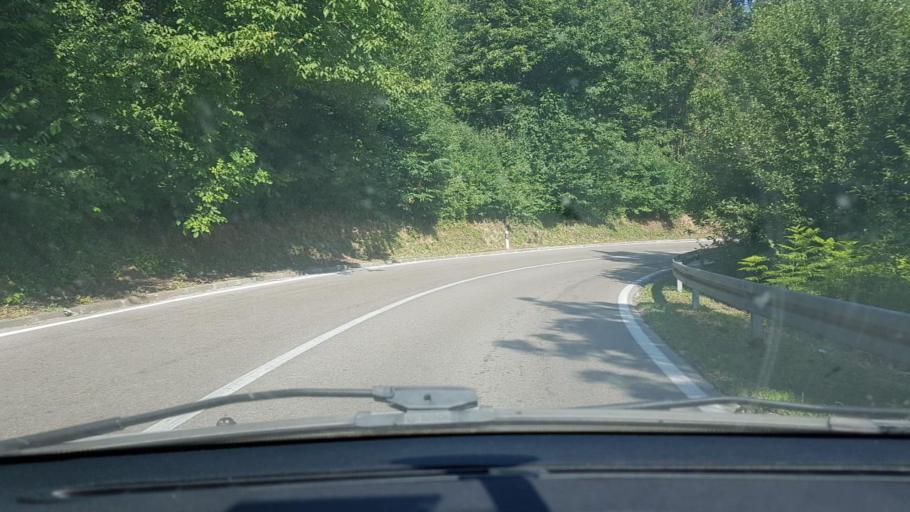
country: BA
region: Federation of Bosnia and Herzegovina
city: Pecigrad
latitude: 45.0490
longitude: 15.9026
